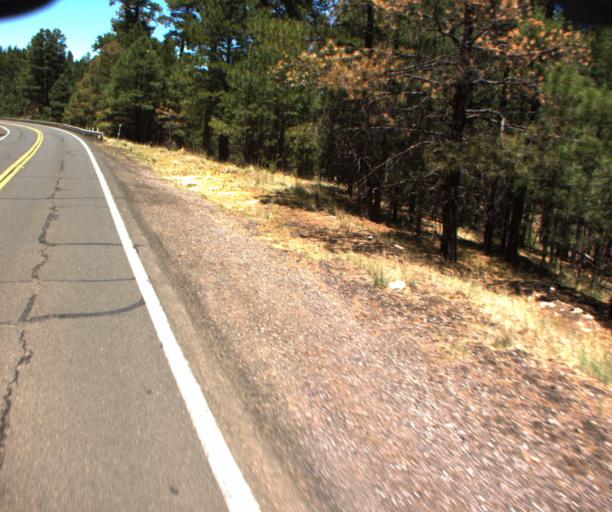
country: US
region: Arizona
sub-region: Gila County
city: Pine
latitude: 34.6060
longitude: -111.2269
